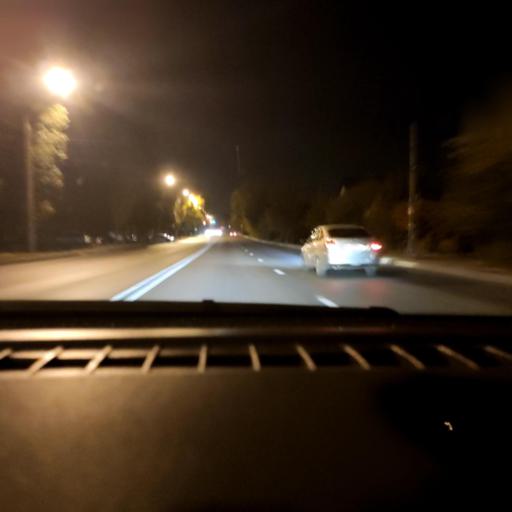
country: RU
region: Voronezj
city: Voronezh
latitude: 51.6948
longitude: 39.1997
